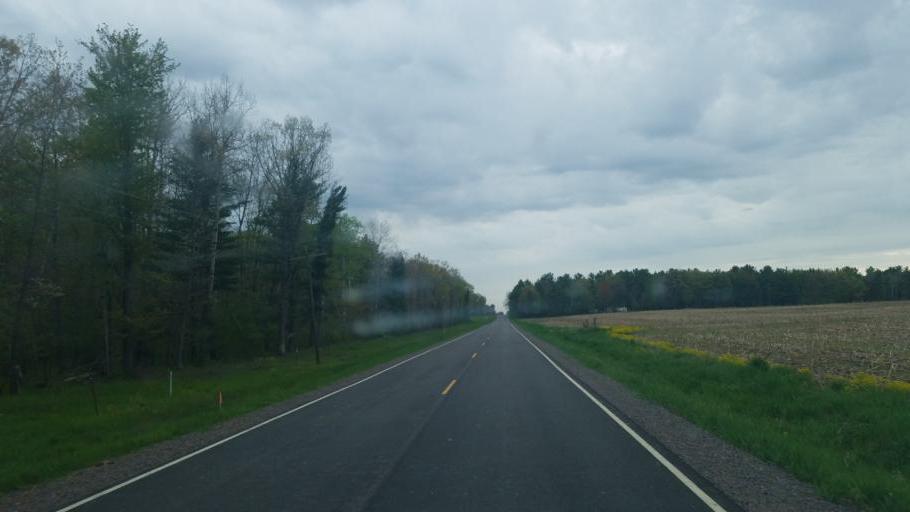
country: US
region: Wisconsin
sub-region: Wood County
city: Marshfield
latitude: 44.4749
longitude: -90.2801
